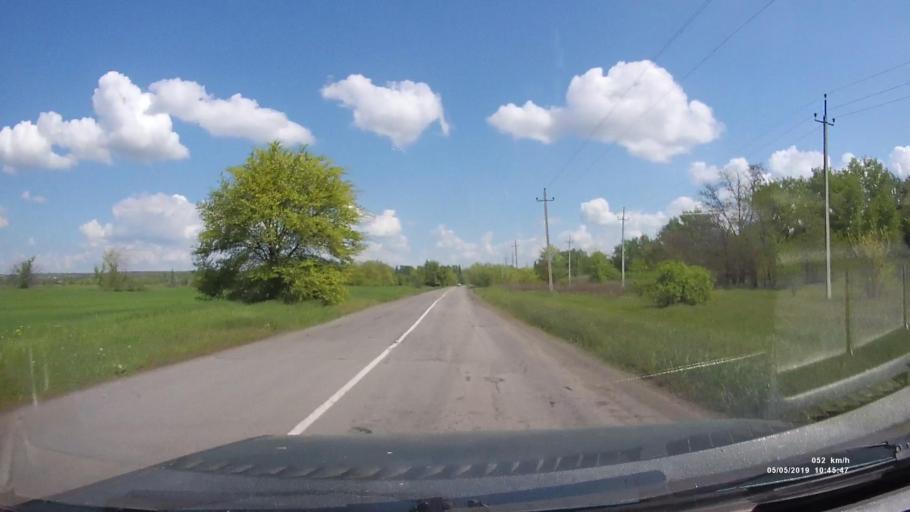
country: RU
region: Rostov
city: Ust'-Donetskiy
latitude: 47.6296
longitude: 40.8397
